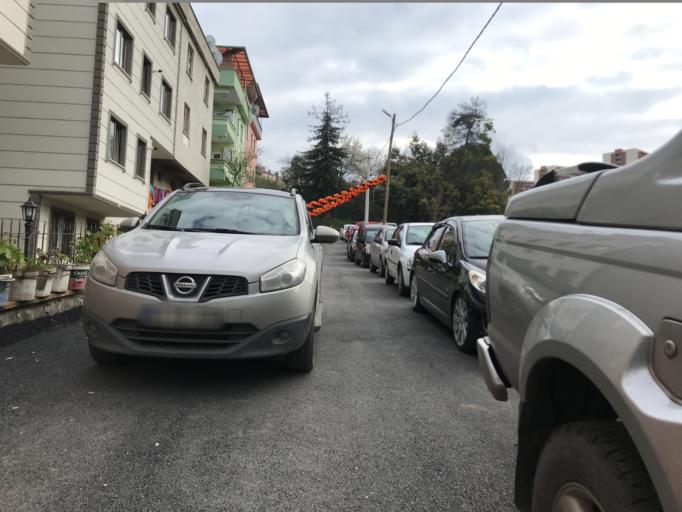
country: TR
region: Trabzon
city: Trabzon
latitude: 40.9912
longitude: 39.7770
